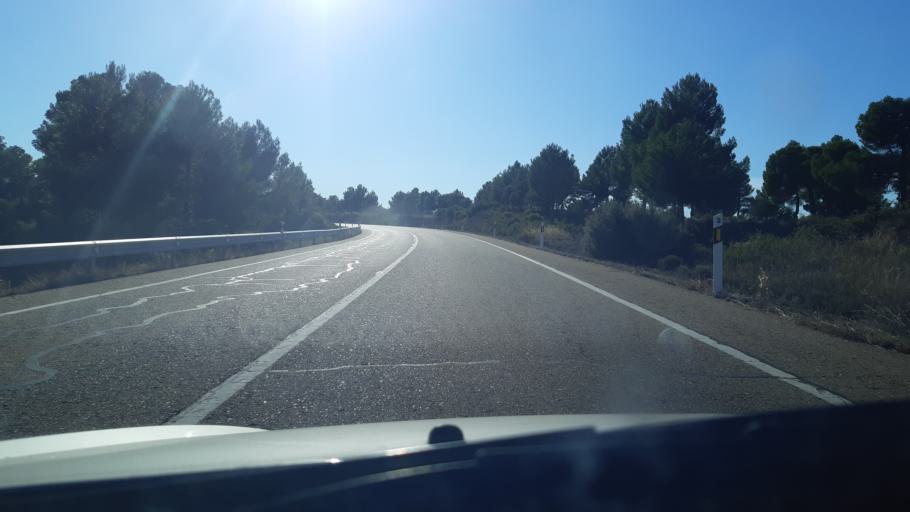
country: ES
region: Aragon
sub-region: Provincia de Teruel
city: Fornoles
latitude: 40.9266
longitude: -0.0164
